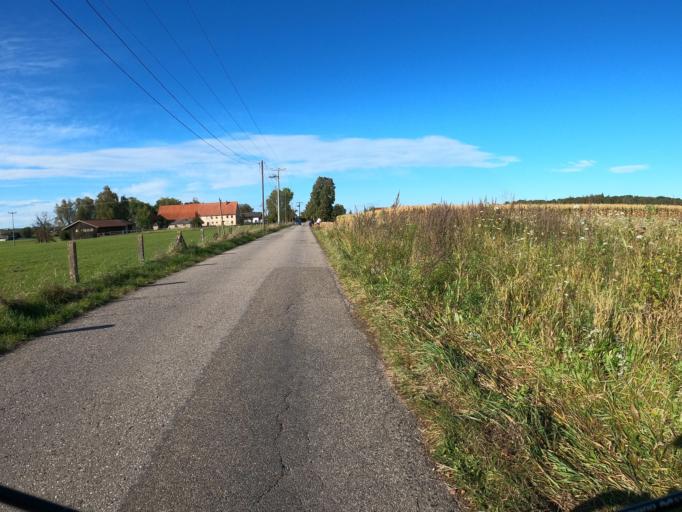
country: DE
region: Bavaria
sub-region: Swabia
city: Nersingen
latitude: 48.4173
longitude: 10.1410
